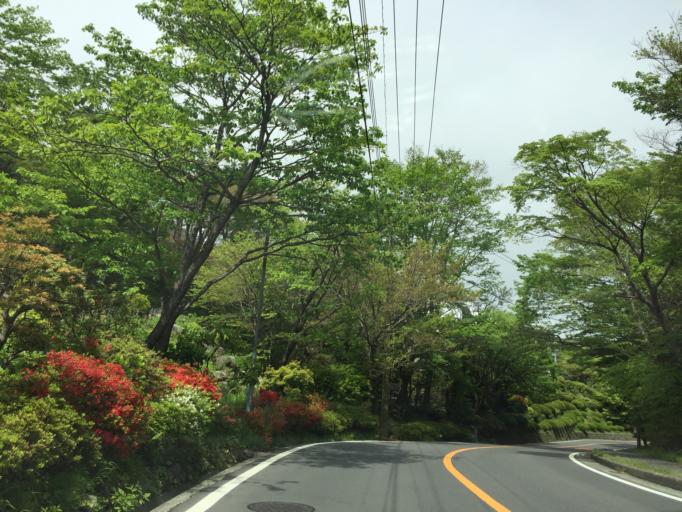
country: JP
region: Kanagawa
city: Hakone
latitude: 35.2470
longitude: 139.0344
